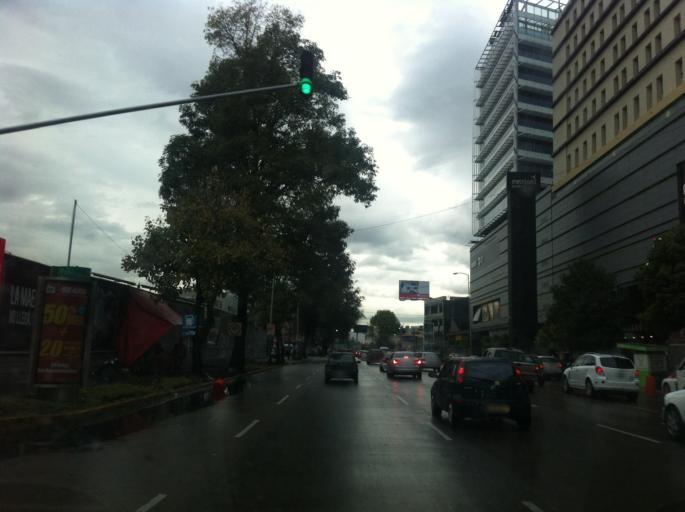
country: MX
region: Mexico City
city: Colonia del Valle
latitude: 19.3958
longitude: -99.1813
